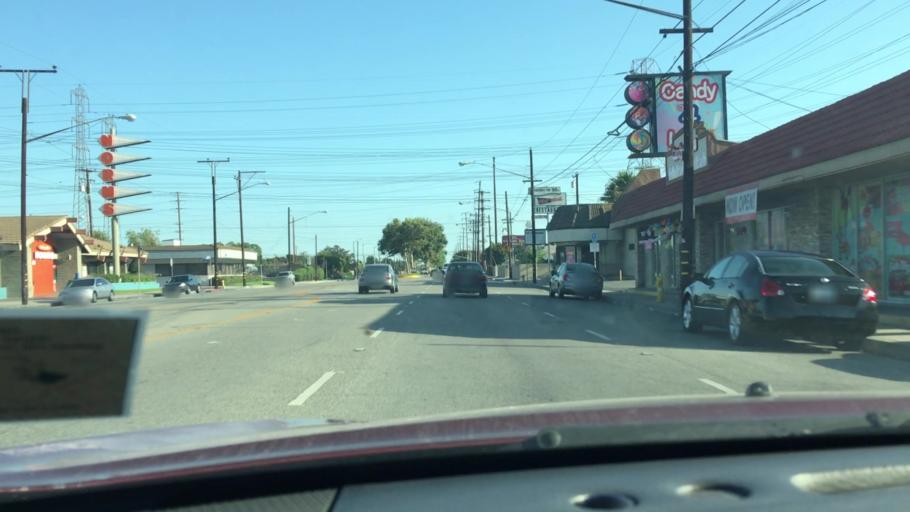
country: US
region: California
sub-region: Los Angeles County
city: Lakewood
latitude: 33.8704
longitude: -118.1427
